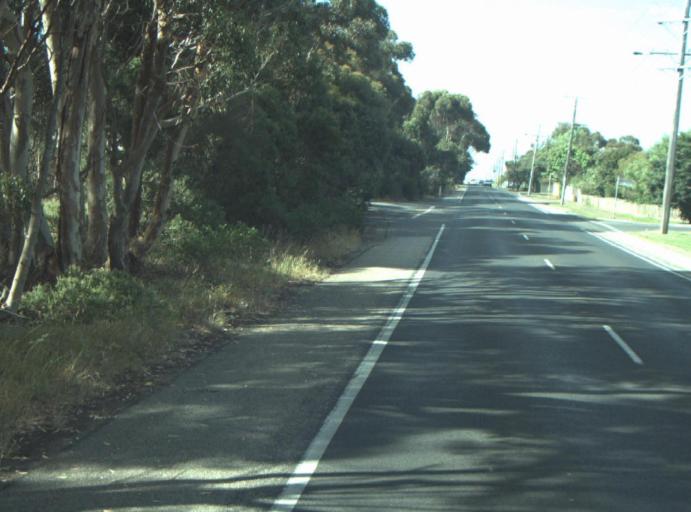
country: AU
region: Victoria
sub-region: Greater Geelong
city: Leopold
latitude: -38.2758
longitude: 144.5313
